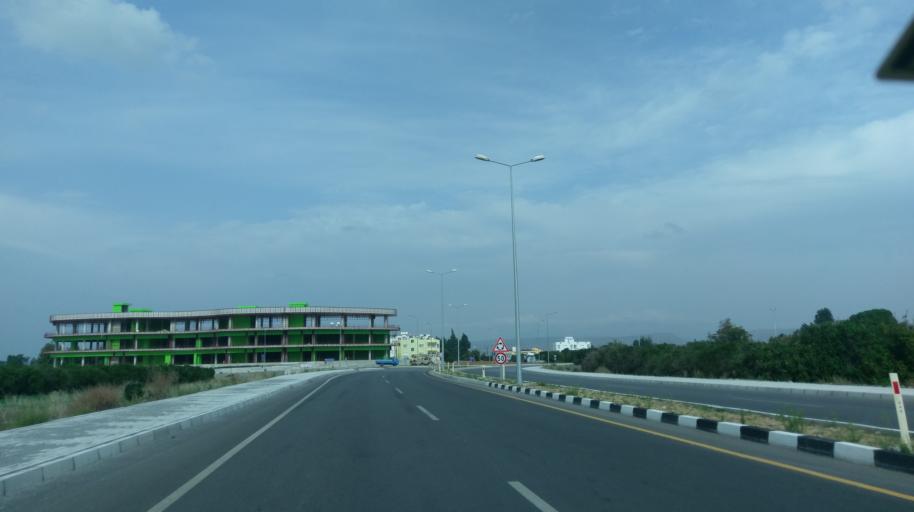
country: CY
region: Lefkosia
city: Morfou
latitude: 35.1895
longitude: 33.0022
